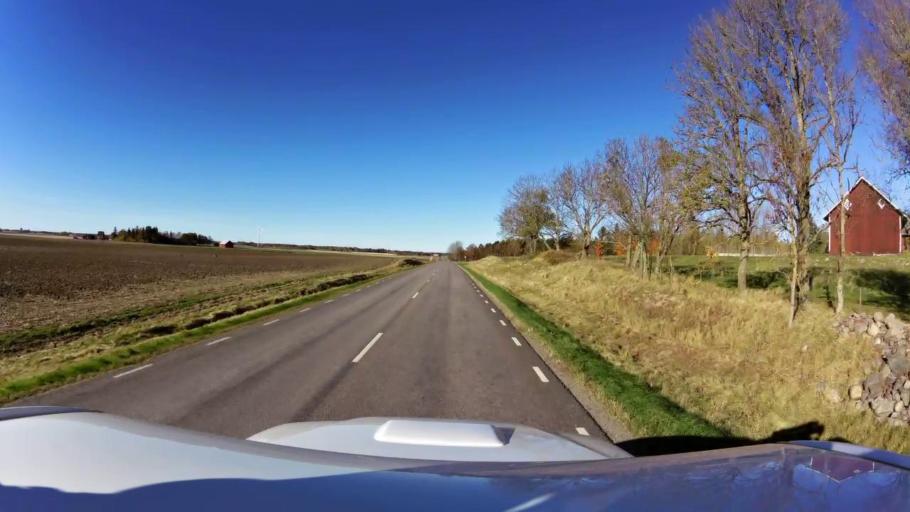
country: SE
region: OEstergoetland
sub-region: Linkopings Kommun
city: Vikingstad
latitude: 58.4823
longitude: 15.3908
